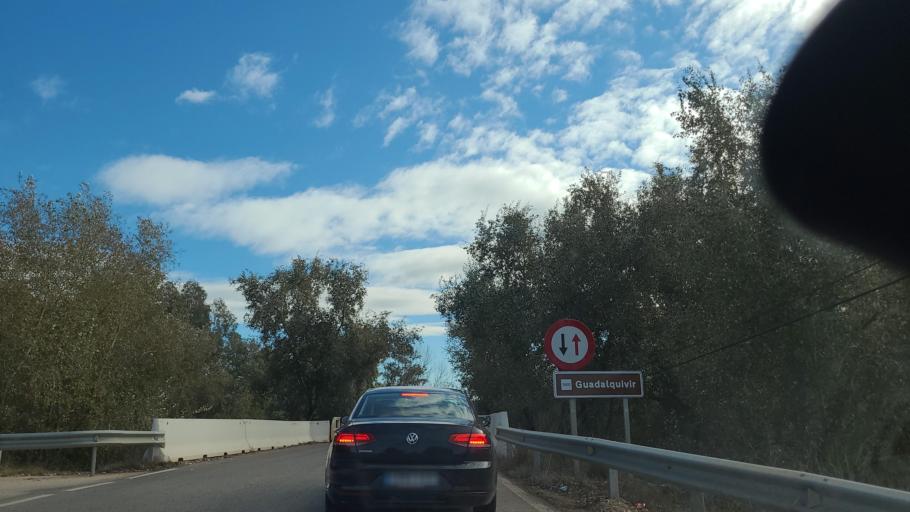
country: ES
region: Andalusia
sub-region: Provincia de Jaen
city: Villanueva de la Reina
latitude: 38.0269
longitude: -3.9163
